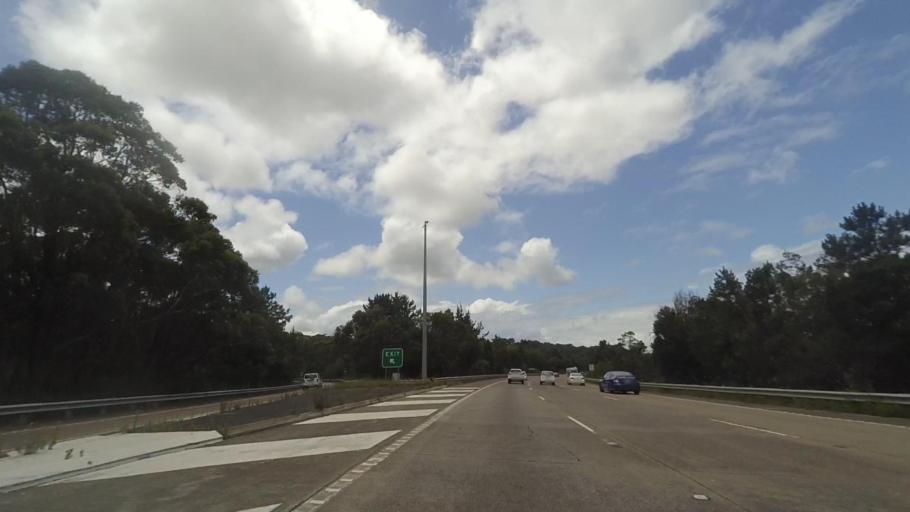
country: AU
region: New South Wales
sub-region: Gosford Shire
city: Narara
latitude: -33.3695
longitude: 151.3088
